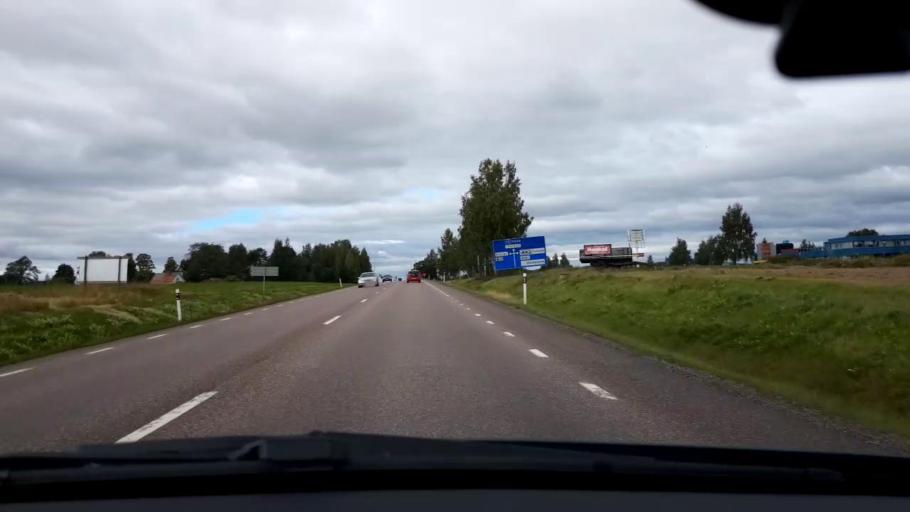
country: SE
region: Dalarna
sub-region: Borlange Kommun
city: Borlaenge
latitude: 60.4601
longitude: 15.4742
